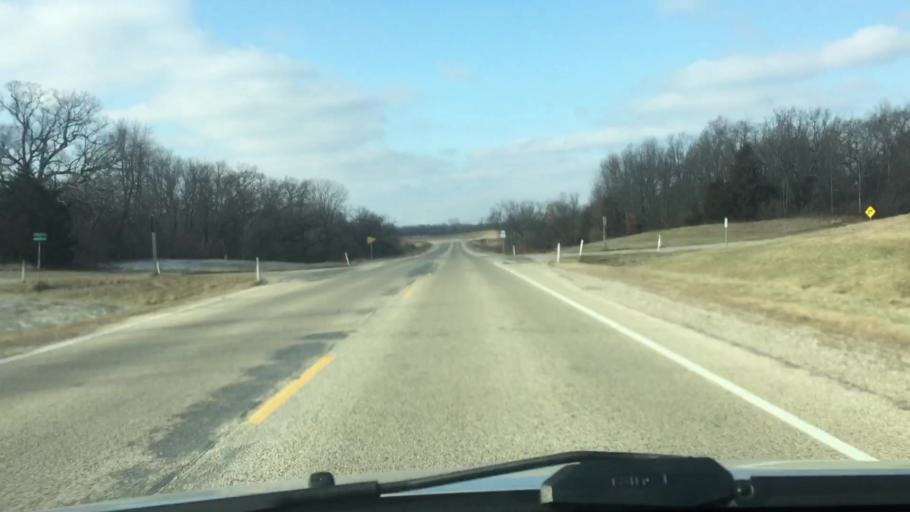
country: US
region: Wisconsin
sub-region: Jefferson County
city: Palmyra
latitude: 42.8827
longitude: -88.5563
